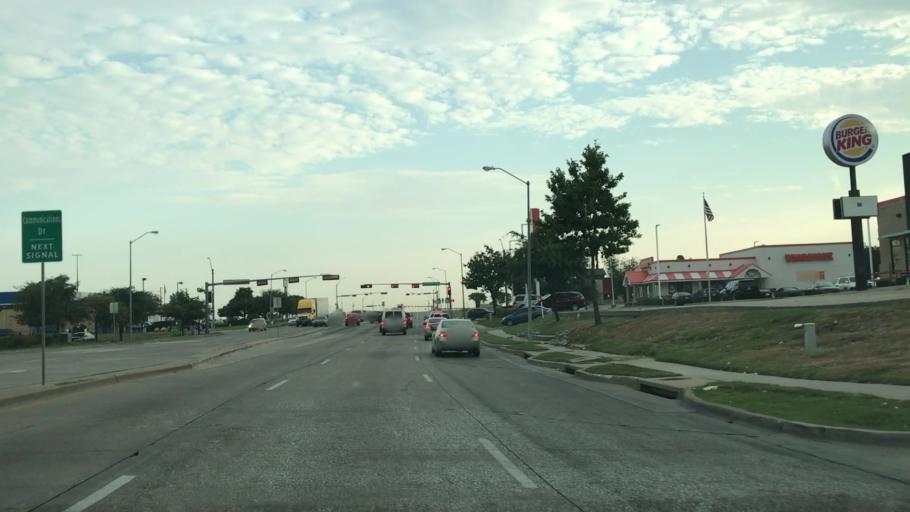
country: US
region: Texas
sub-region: Dallas County
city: Cockrell Hill
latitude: 32.7636
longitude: -96.8953
